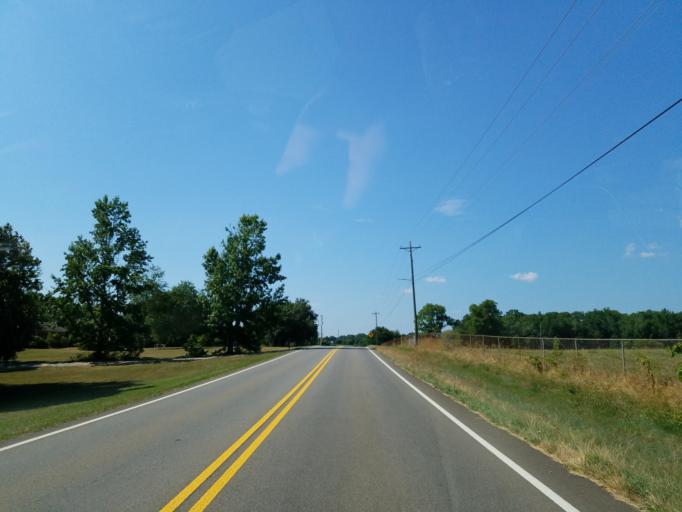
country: US
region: Georgia
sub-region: Fulton County
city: Milton
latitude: 34.2278
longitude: -84.2898
